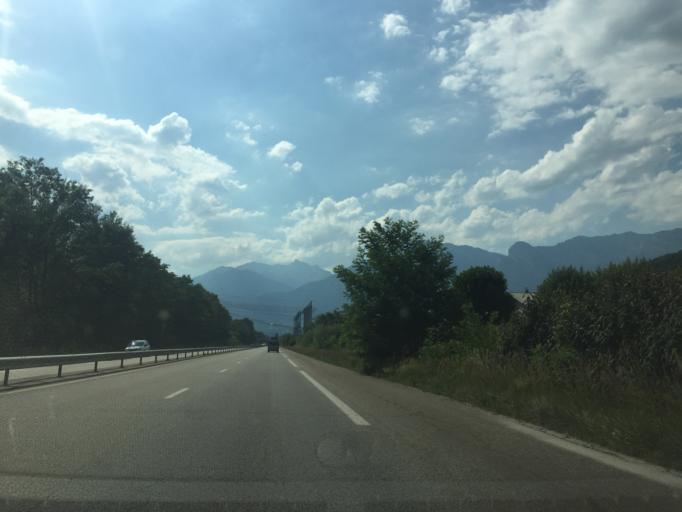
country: FR
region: Rhone-Alpes
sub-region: Departement de la Savoie
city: Albertville
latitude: 45.6593
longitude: 6.4257
